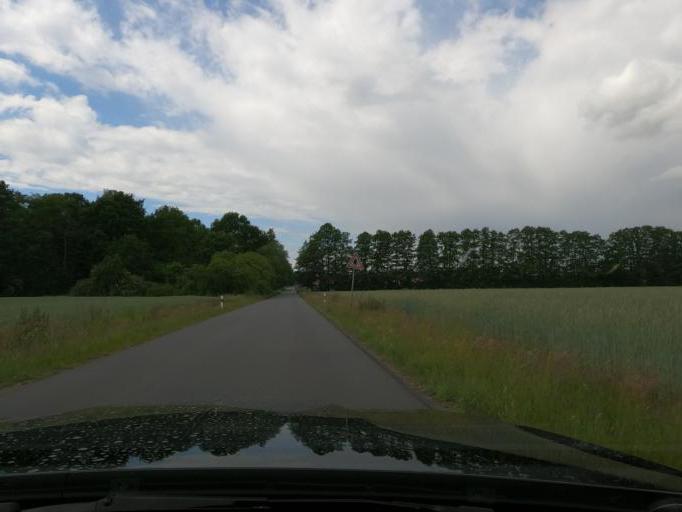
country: DE
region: Lower Saxony
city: Steimbke
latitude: 52.6425
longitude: 9.4499
